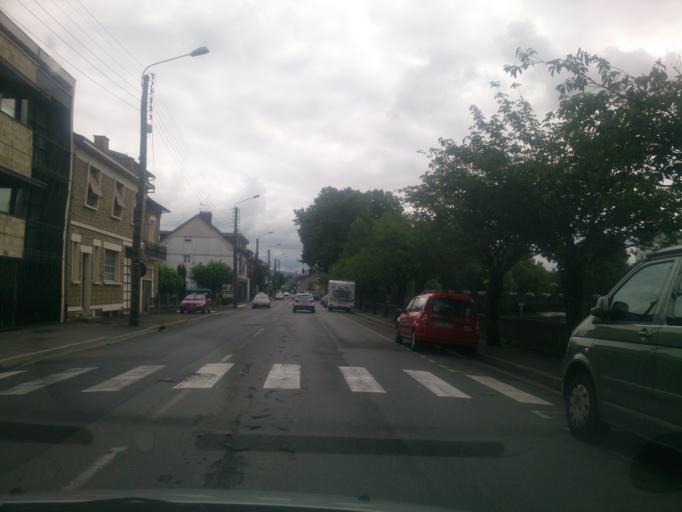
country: FR
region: Limousin
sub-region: Departement de la Correze
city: Brive-la-Gaillarde
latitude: 45.1653
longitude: 1.5353
